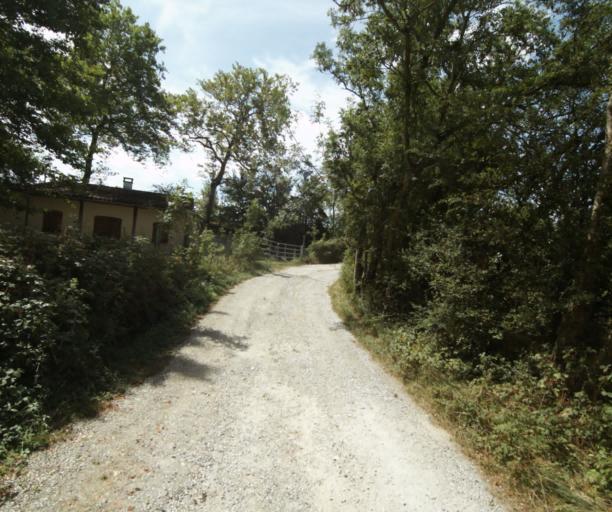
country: FR
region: Midi-Pyrenees
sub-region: Departement du Tarn
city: Dourgne
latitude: 43.4821
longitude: 2.1162
